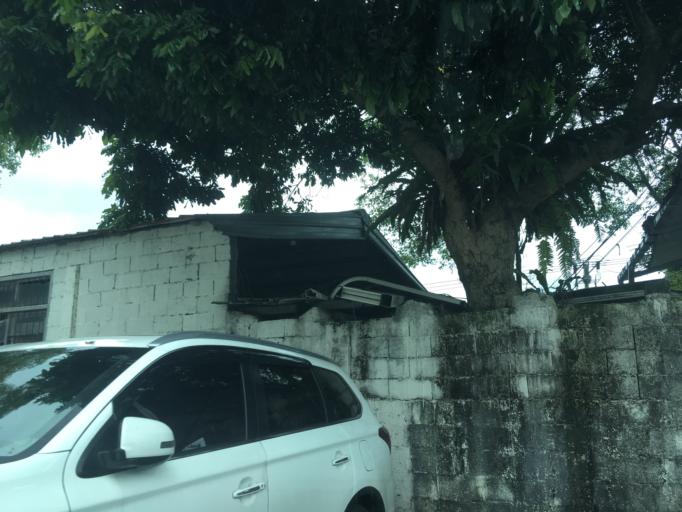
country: TW
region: Taiwan
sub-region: Hualien
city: Hualian
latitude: 23.9740
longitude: 121.5642
